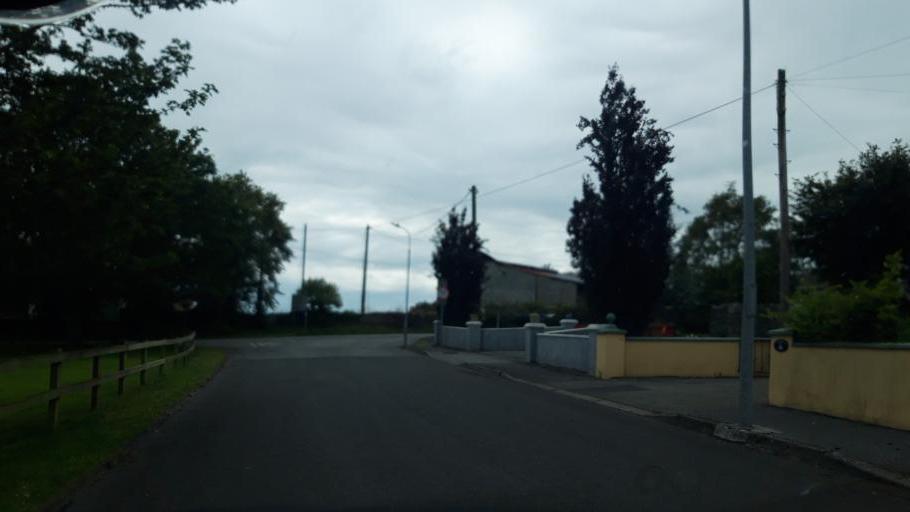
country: IE
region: Leinster
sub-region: Kilkenny
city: Ballyragget
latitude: 52.7901
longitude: -7.3351
